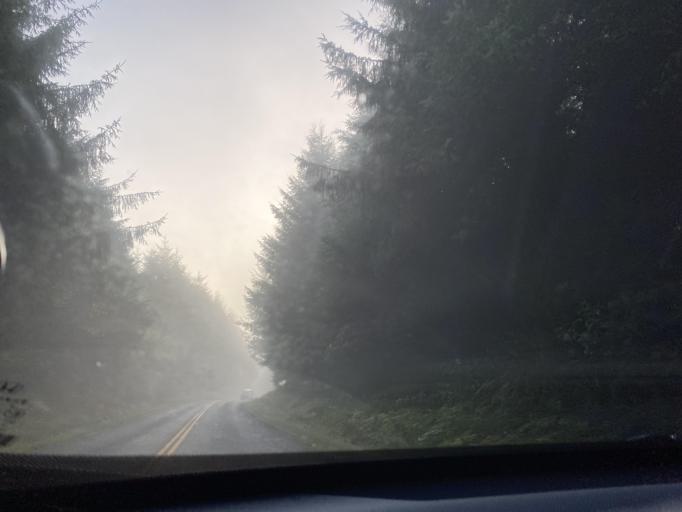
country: US
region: Washington
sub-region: Clallam County
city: Forks
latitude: 47.8095
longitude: -124.0896
